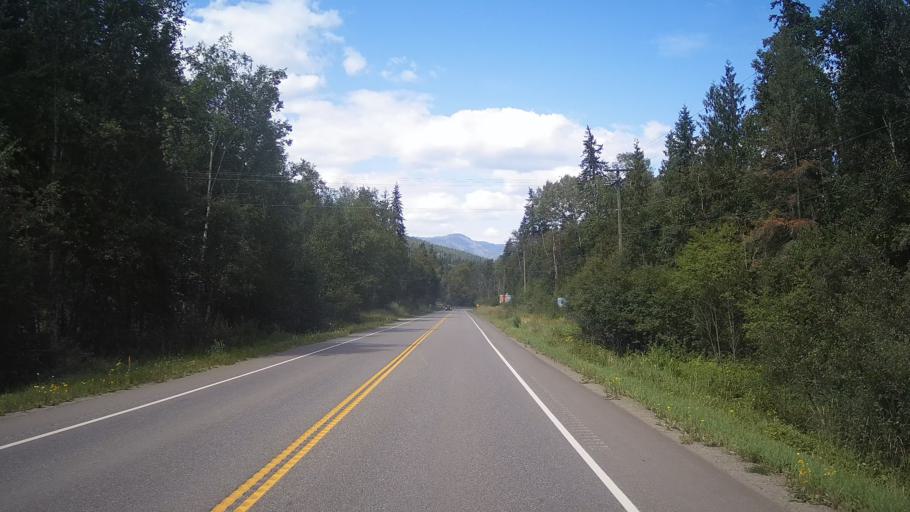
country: CA
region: British Columbia
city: Kamloops
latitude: 51.4107
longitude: -120.2116
